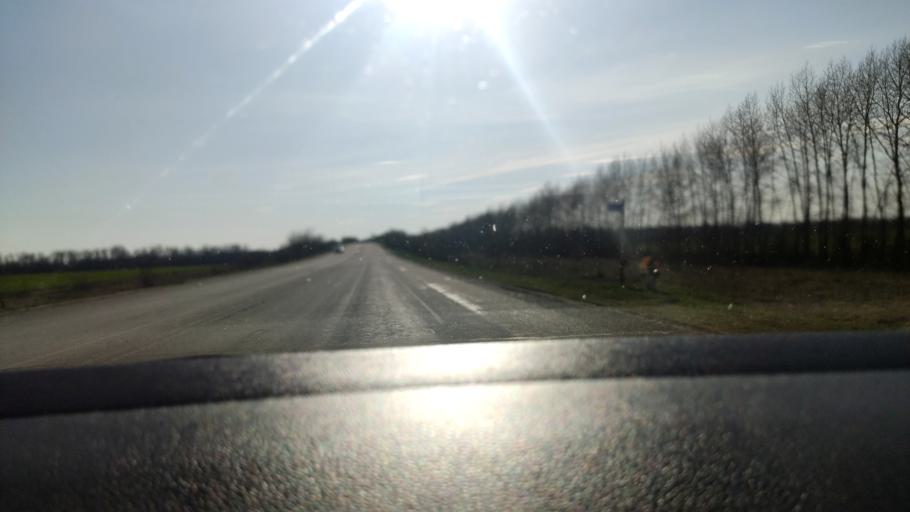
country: RU
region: Voronezj
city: Kolodeznyy
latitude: 51.4121
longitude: 39.2564
